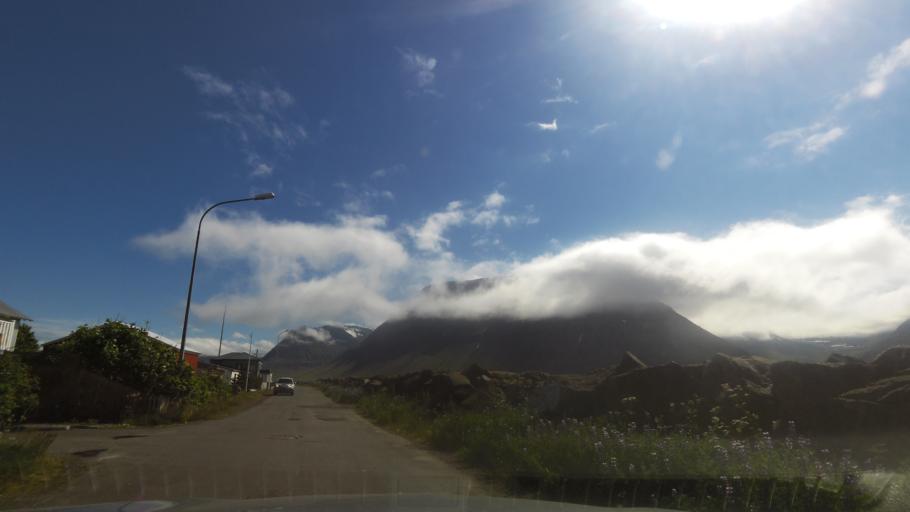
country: IS
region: Westfjords
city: Isafjoerdur
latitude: 66.0481
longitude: -23.5146
